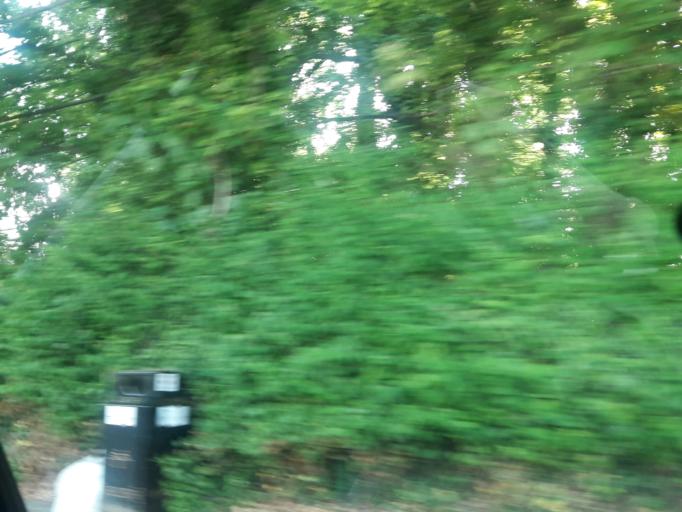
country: IE
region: Leinster
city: Hartstown
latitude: 53.3835
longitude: -6.4095
